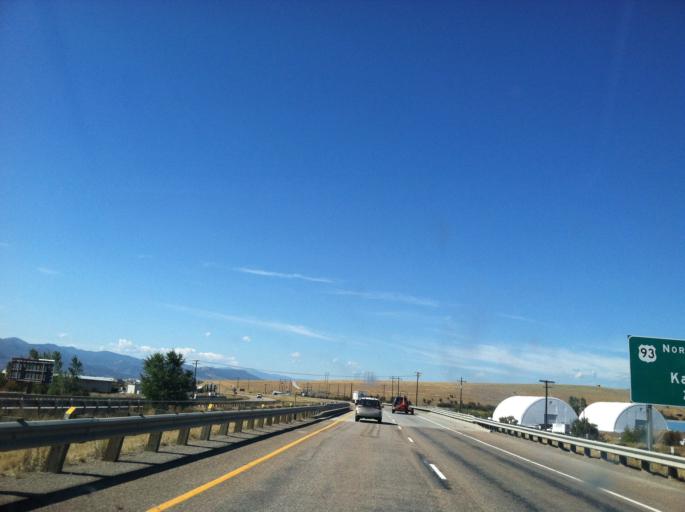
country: US
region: Montana
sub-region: Missoula County
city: Orchard Homes
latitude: 46.9357
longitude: -114.0929
